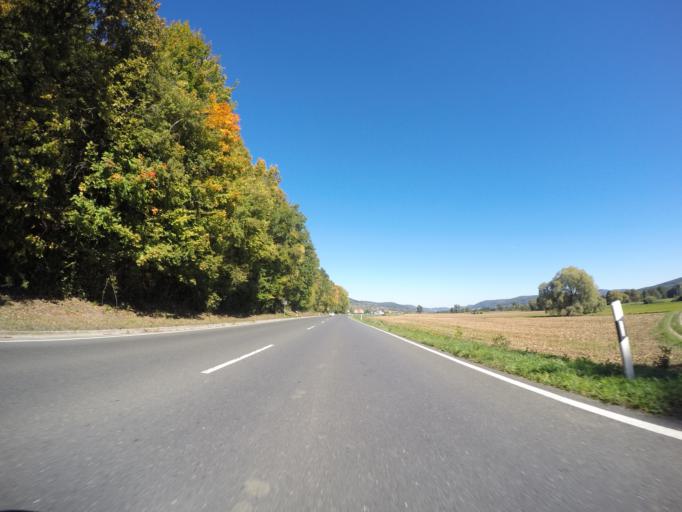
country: DE
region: Bavaria
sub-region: Upper Franconia
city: Wiesenthau
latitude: 49.7357
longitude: 11.1305
